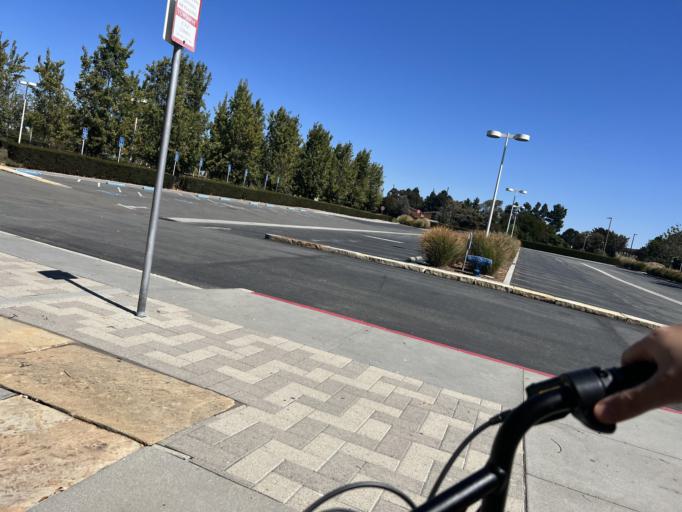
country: US
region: California
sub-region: San Mateo County
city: Redwood Shores
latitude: 37.5295
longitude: -122.2619
